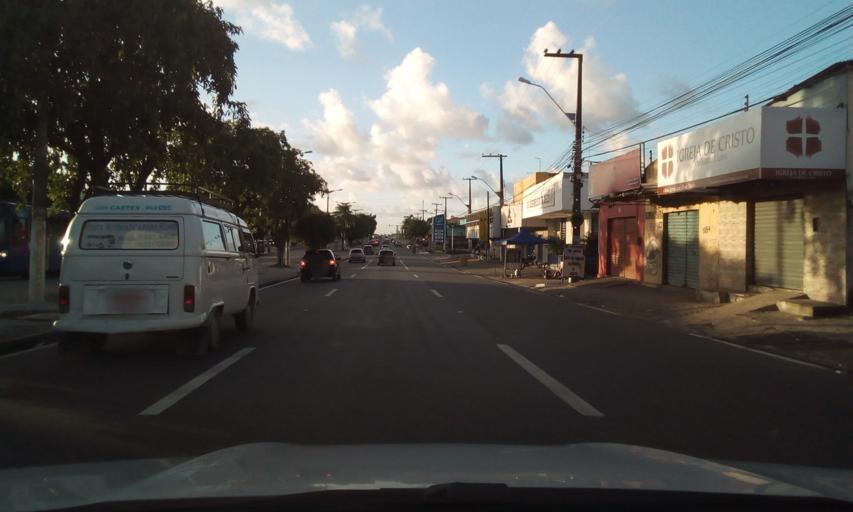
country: BR
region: Pernambuco
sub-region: Abreu E Lima
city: Abreu e Lima
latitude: -7.8980
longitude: -34.9024
